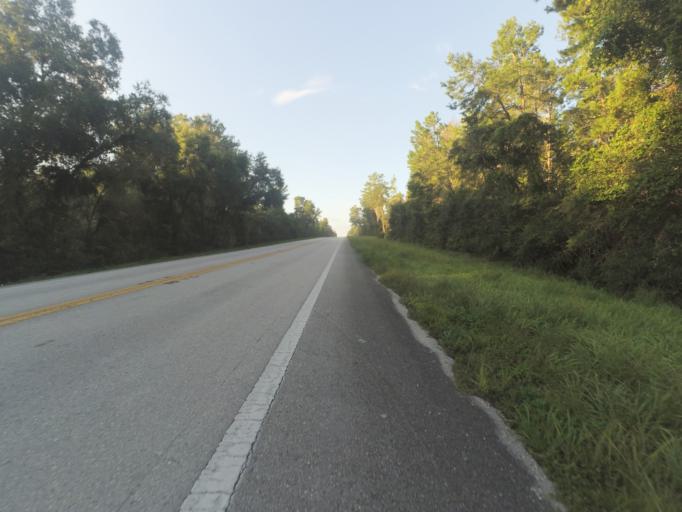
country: US
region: Florida
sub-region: Lake County
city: Astor
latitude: 29.2660
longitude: -81.6466
